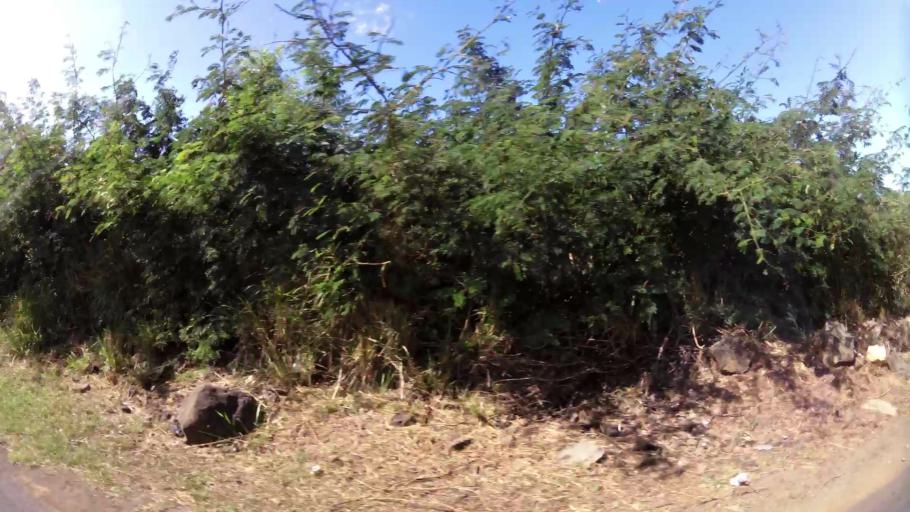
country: MU
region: Black River
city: Cascavelle
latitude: -20.2696
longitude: 57.4157
